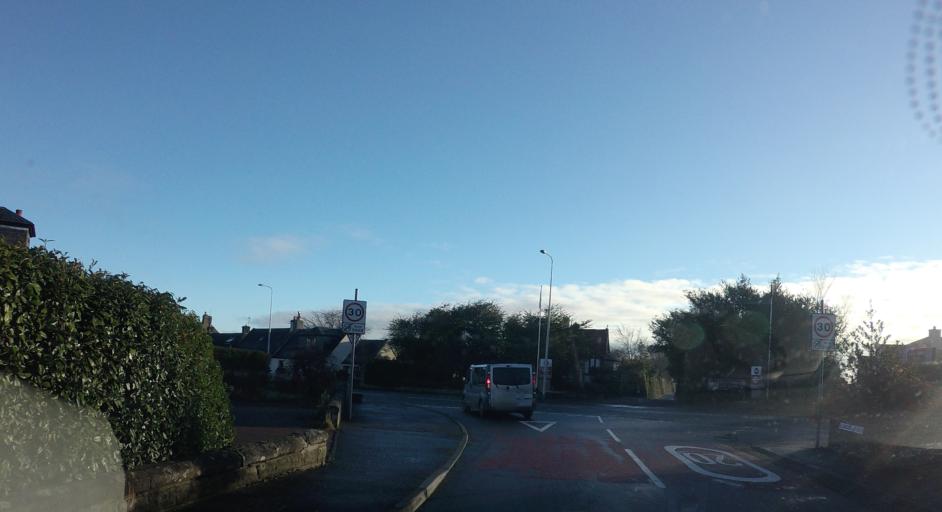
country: GB
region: Scotland
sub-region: Fife
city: Crossford
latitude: 56.0636
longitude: -3.4997
